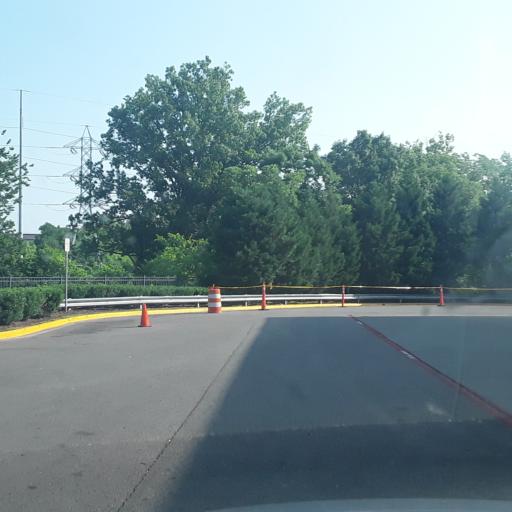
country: US
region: Tennessee
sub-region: Williamson County
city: Brentwood Estates
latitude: 36.0426
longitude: -86.7098
